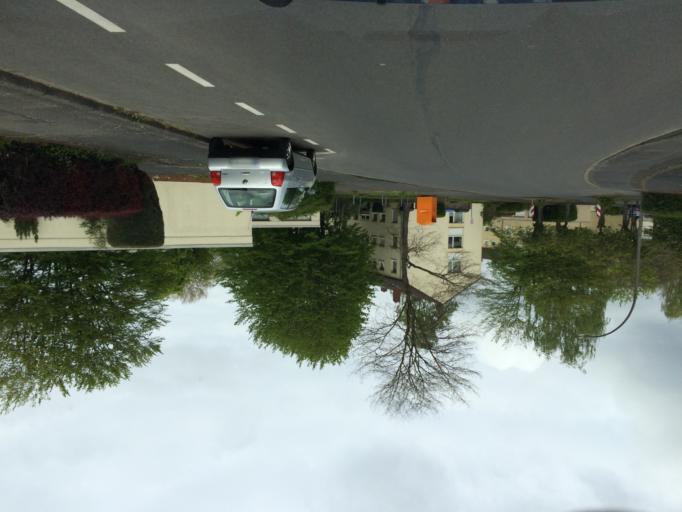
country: DE
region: North Rhine-Westphalia
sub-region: Regierungsbezirk Koln
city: Konigswinter
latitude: 50.6694
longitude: 7.1686
